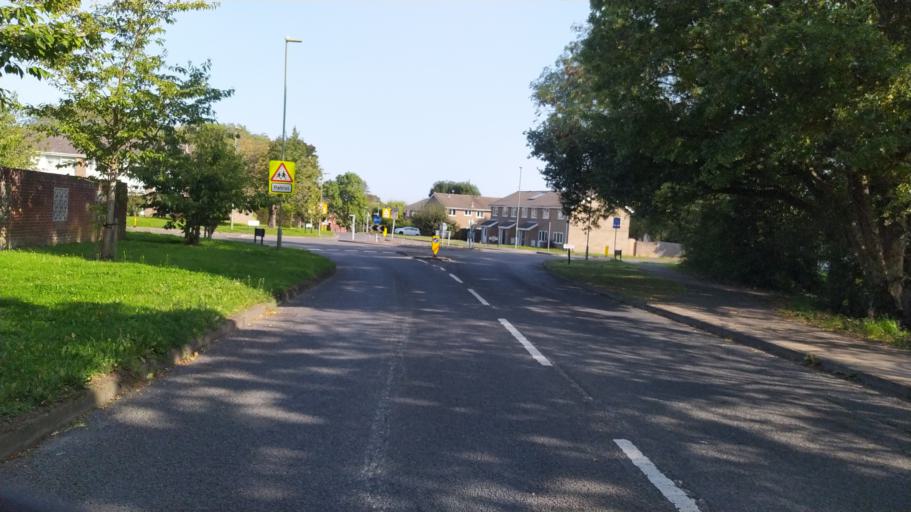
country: GB
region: England
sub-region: Hampshire
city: Hedge End
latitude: 50.9045
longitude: -1.2979
